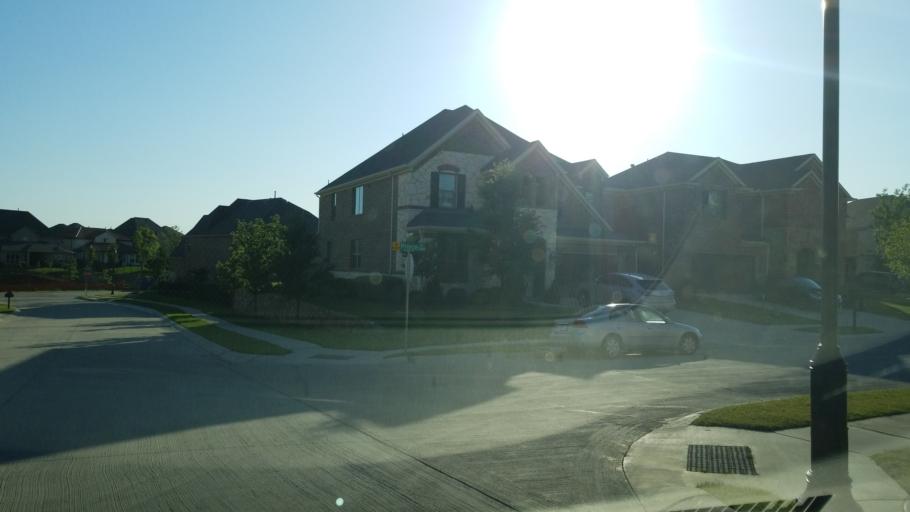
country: US
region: Texas
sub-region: Dallas County
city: Coppell
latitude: 32.9085
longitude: -96.9849
